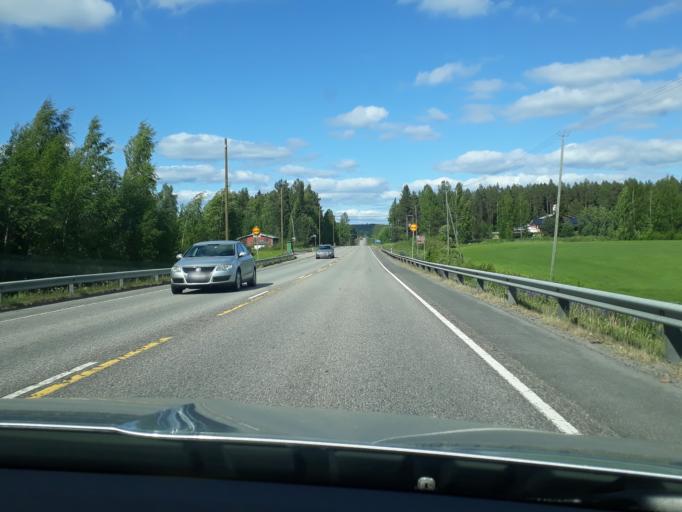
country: FI
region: Central Finland
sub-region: AEaenekoski
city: AEaenekoski
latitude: 62.6540
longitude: 25.7223
